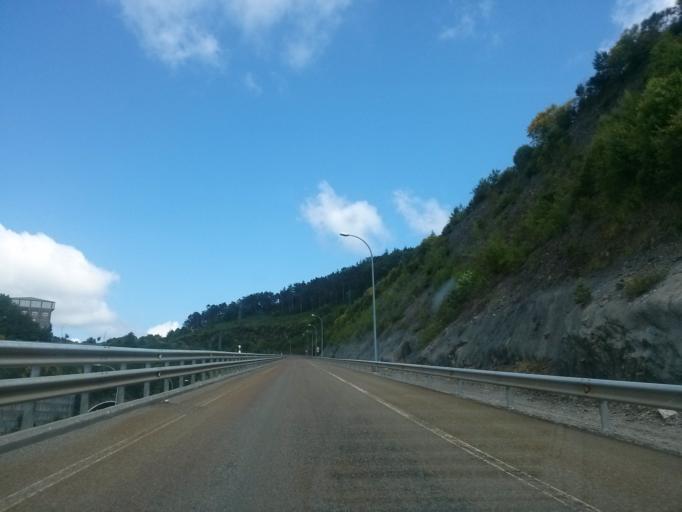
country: ES
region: Castille and Leon
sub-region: Provincia de Leon
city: Balboa
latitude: 42.7259
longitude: -7.0305
